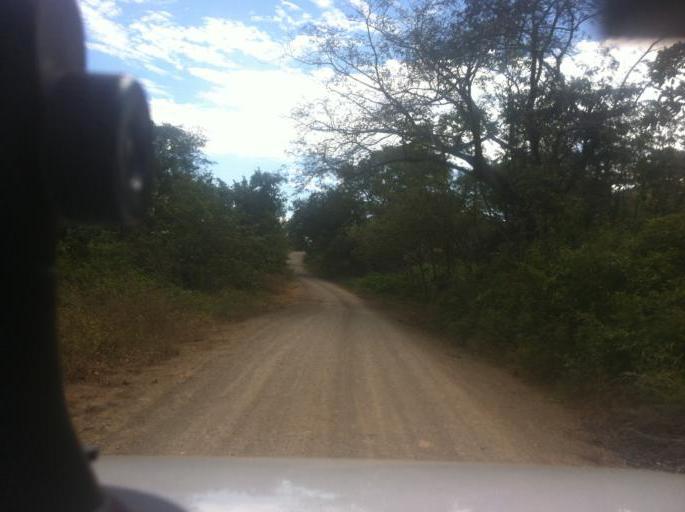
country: NI
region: Granada
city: Nandaime
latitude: 11.5971
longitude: -86.0269
